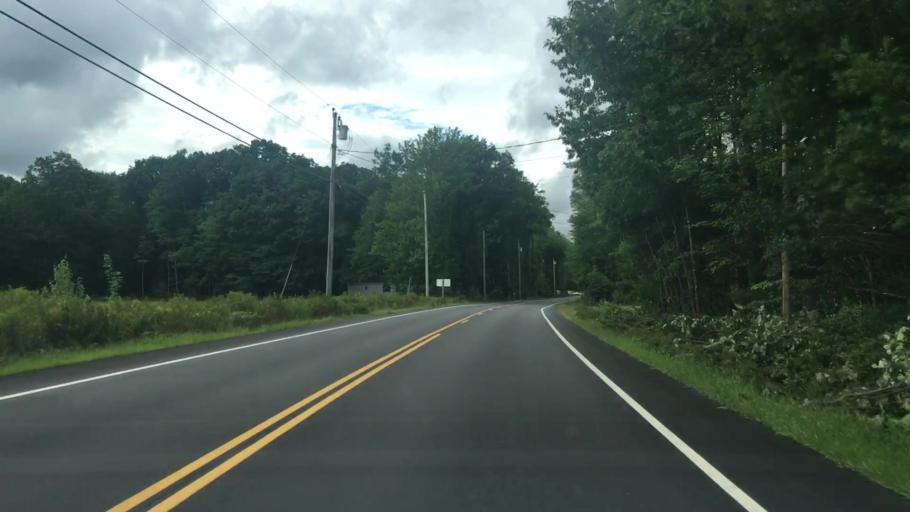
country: US
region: Maine
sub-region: York County
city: West Kennebunk
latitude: 43.4754
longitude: -70.6033
